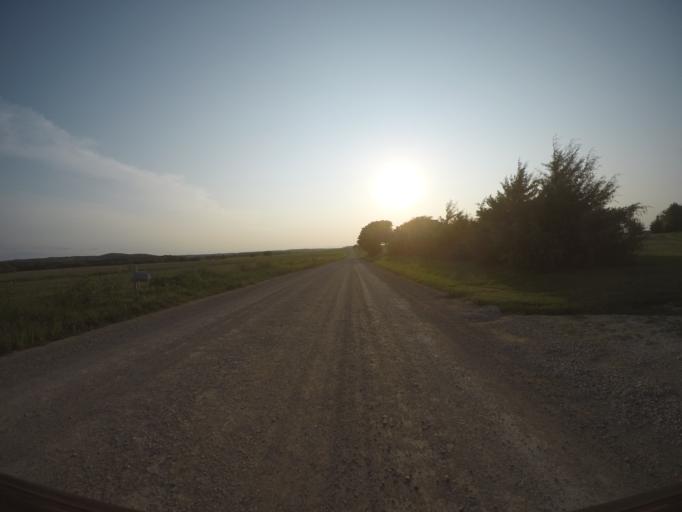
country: US
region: Kansas
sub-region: Riley County
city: Manhattan
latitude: 39.1304
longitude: -96.4492
